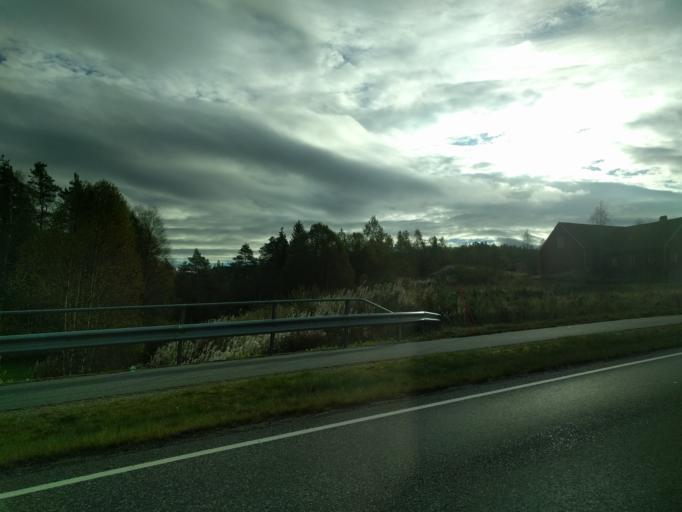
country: NO
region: Vest-Agder
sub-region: Kristiansand
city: Strai
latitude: 58.2879
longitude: 7.8432
